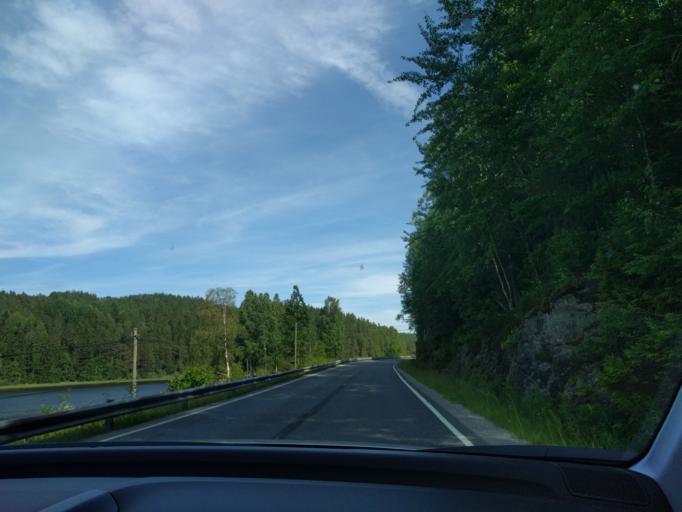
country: NO
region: Aust-Agder
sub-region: Gjerstad
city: Gjerstad
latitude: 58.8516
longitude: 9.0816
